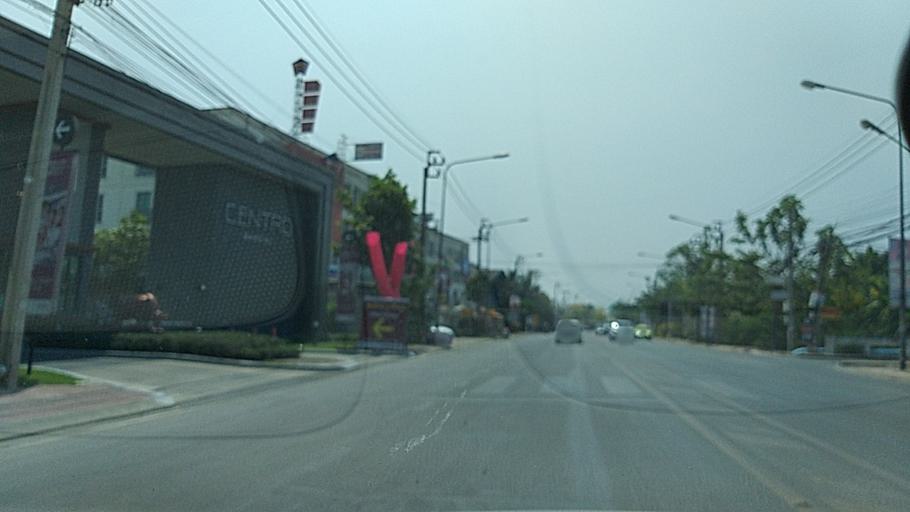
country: TH
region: Nonthaburi
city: Bang Bua Thong
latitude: 13.9101
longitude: 100.3653
